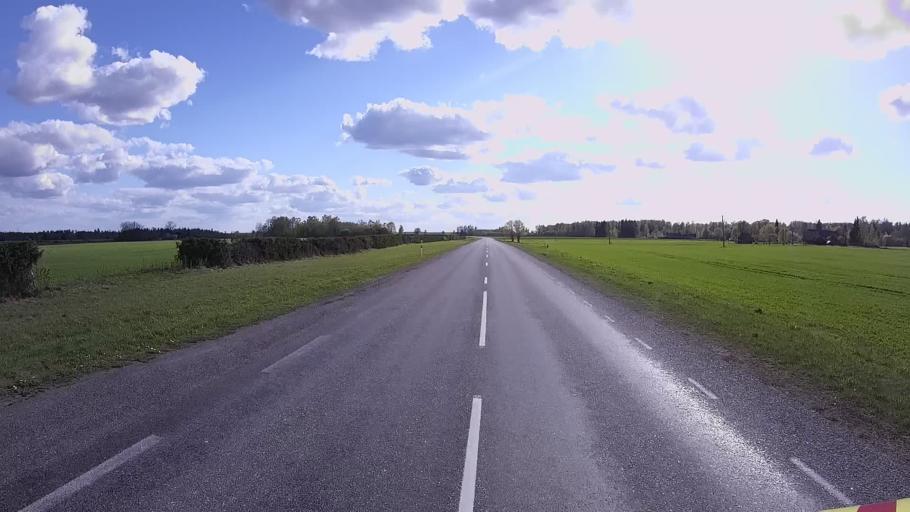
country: EE
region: Jogevamaa
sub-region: Poltsamaa linn
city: Poltsamaa
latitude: 58.6998
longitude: 26.1446
